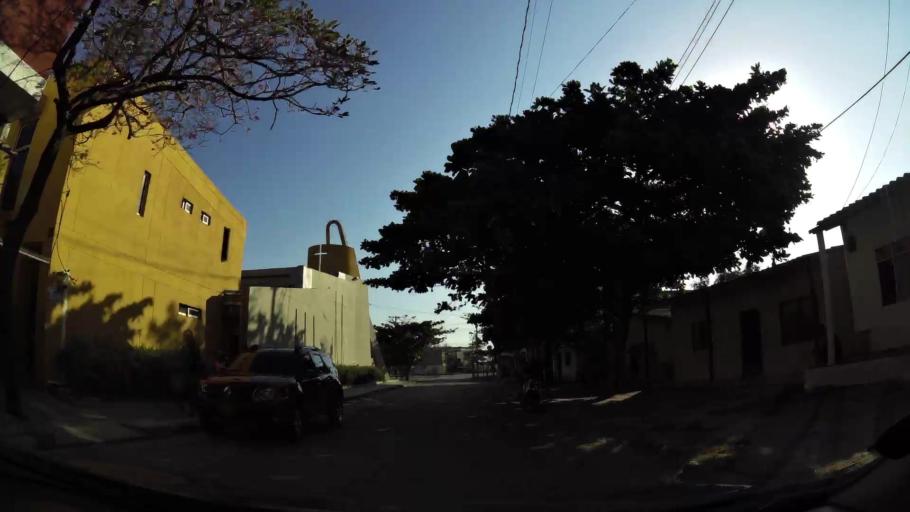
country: CO
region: Atlantico
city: Barranquilla
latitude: 11.0388
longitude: -74.8250
